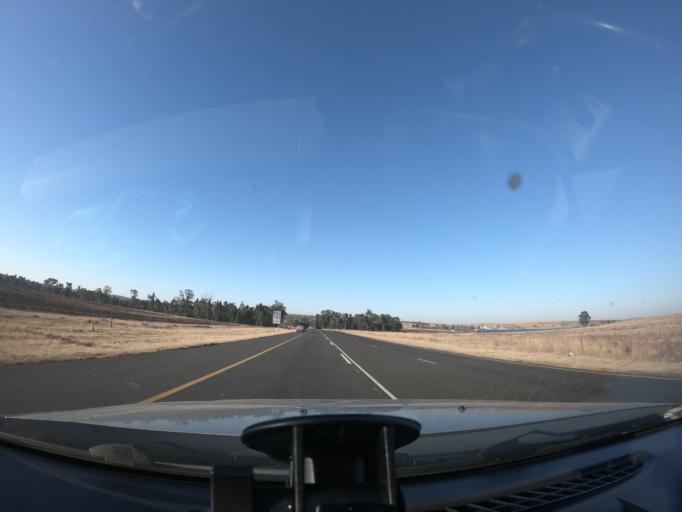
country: ZA
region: Mpumalanga
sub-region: Gert Sibande District Municipality
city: Ermelo
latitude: -26.4589
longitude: 29.9517
